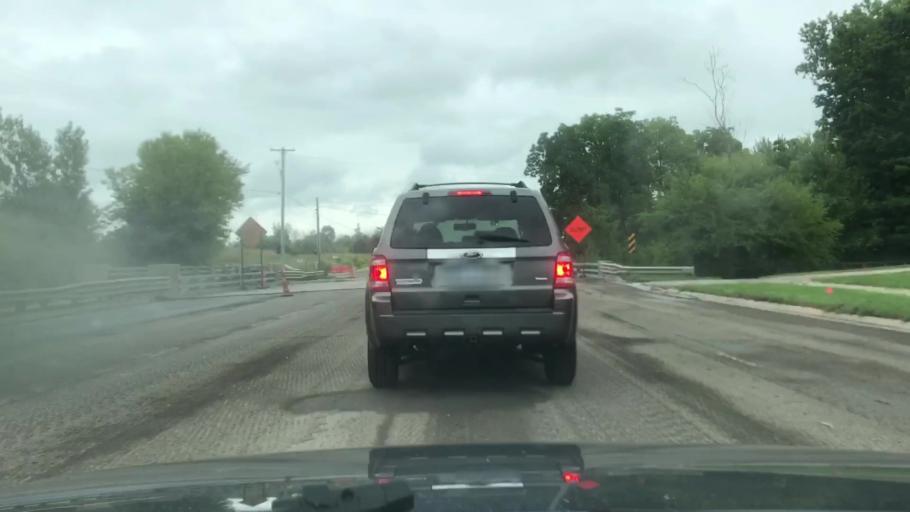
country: US
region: Michigan
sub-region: Ottawa County
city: Zeeland
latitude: 42.7833
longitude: -86.0363
